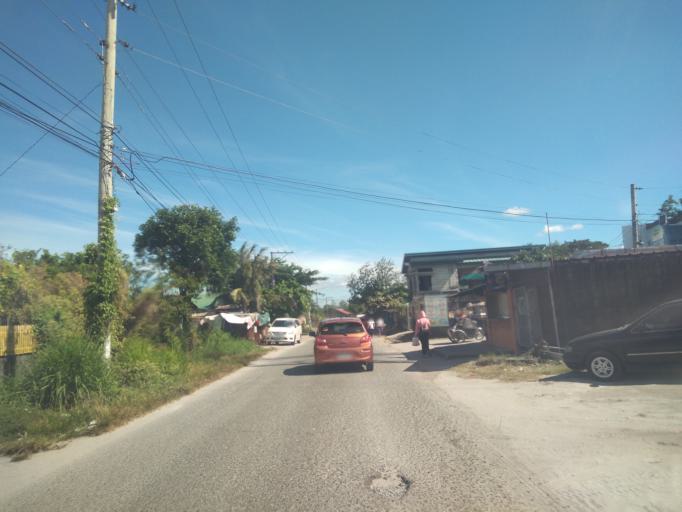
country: PH
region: Central Luzon
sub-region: Province of Pampanga
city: Bacolor
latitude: 15.0022
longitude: 120.6467
